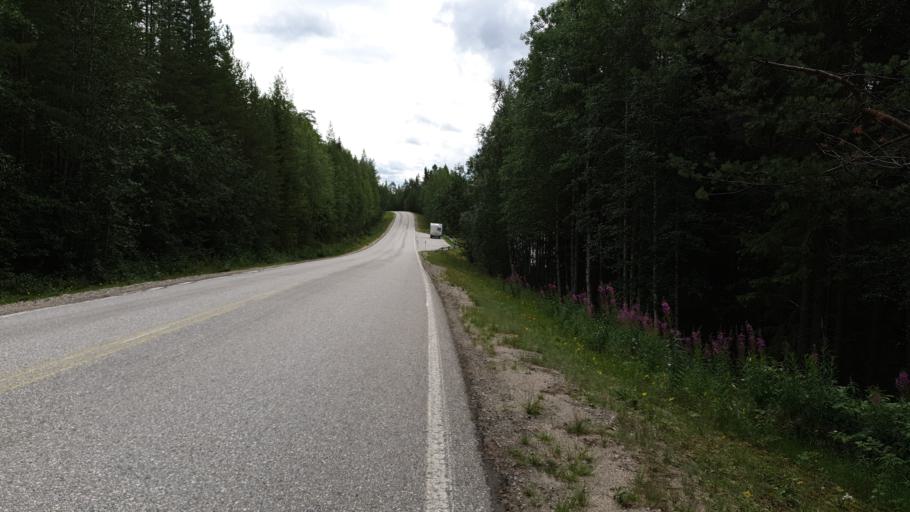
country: FI
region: Kainuu
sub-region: Kehys-Kainuu
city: Kuhmo
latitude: 64.4562
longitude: 29.7700
